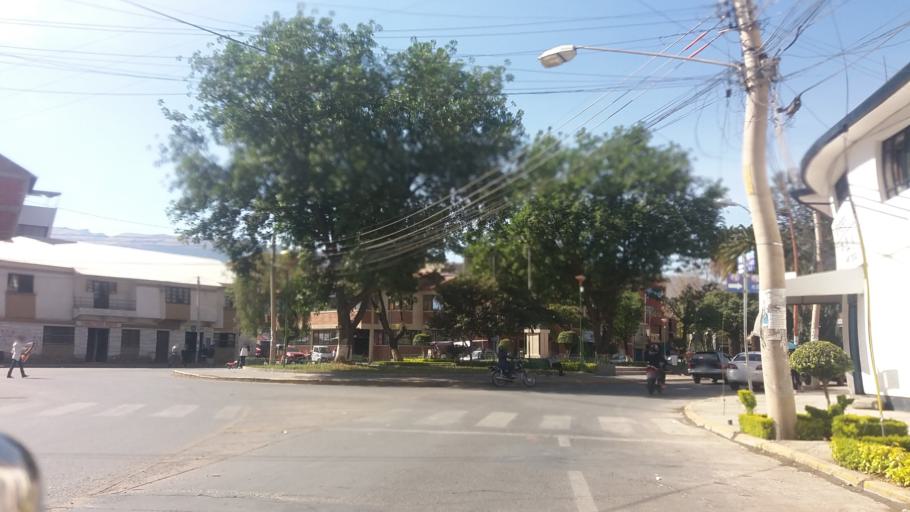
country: BO
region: Cochabamba
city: Cochabamba
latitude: -17.3976
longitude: -66.1630
